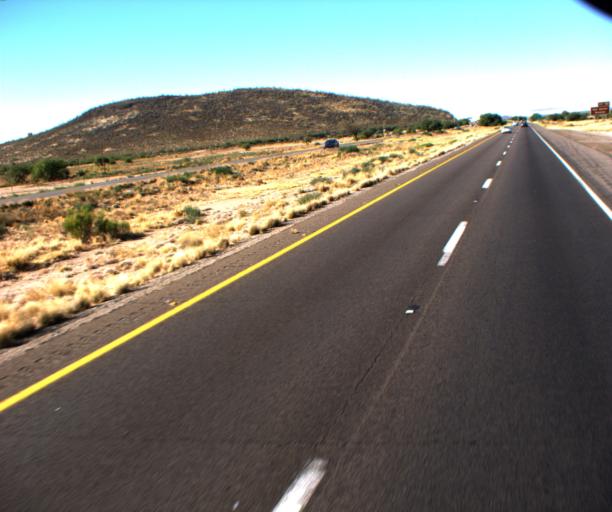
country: US
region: Arizona
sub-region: Pima County
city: Drexel Heights
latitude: 32.1169
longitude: -110.9901
